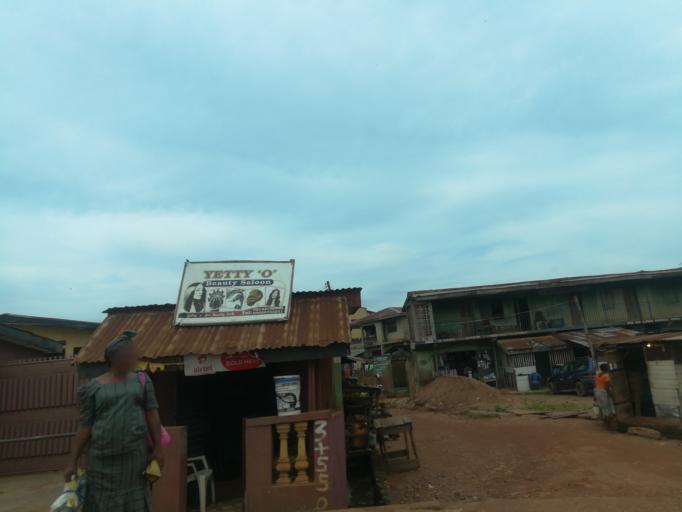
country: NG
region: Oyo
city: Ibadan
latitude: 7.3766
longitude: 3.9539
